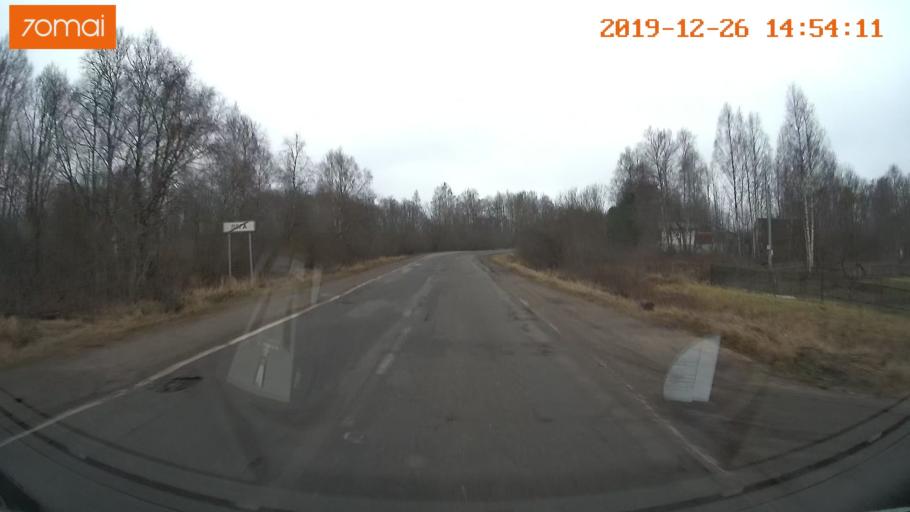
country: RU
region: Jaroslavl
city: Rybinsk
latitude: 58.3091
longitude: 38.8859
